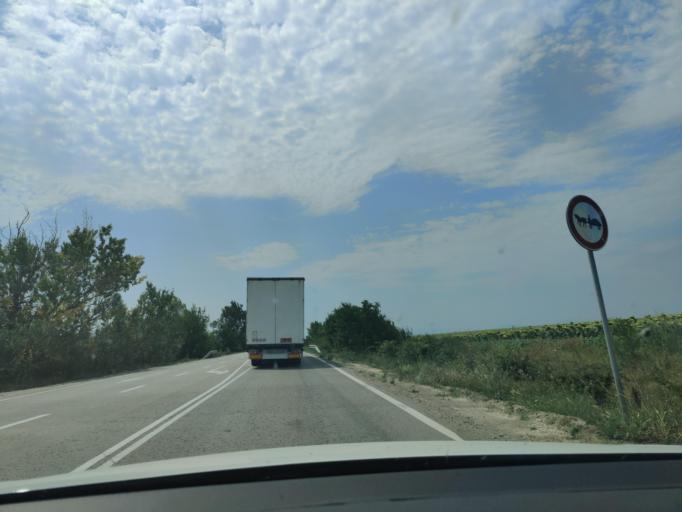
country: BG
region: Vidin
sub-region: Obshtina Vidin
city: Dunavtsi
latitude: 43.8639
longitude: 22.7820
